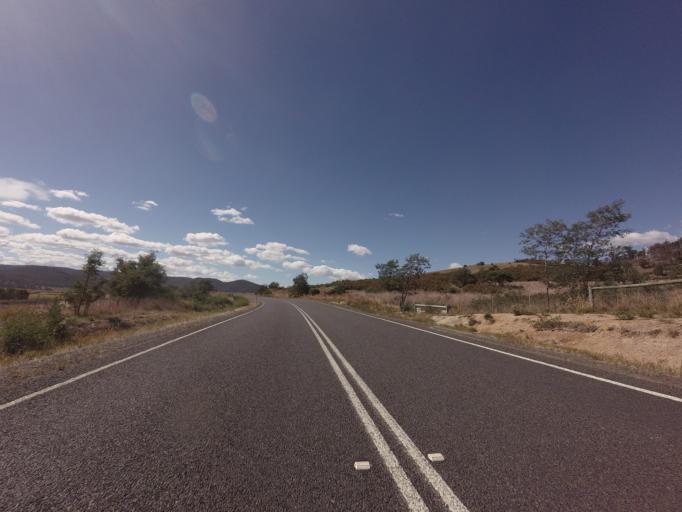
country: AU
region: Tasmania
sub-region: Break O'Day
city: St Helens
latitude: -41.6973
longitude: 147.8618
